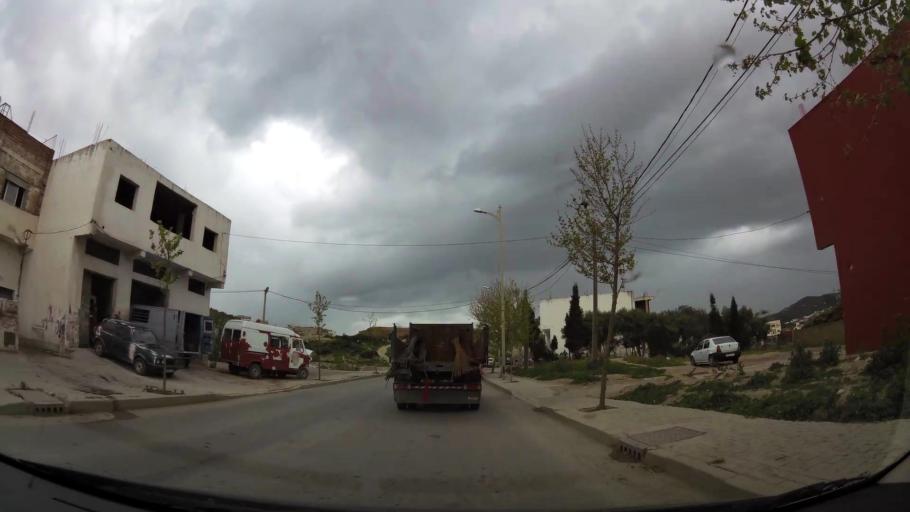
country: MA
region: Tanger-Tetouan
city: Tetouan
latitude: 35.5554
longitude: -5.4013
